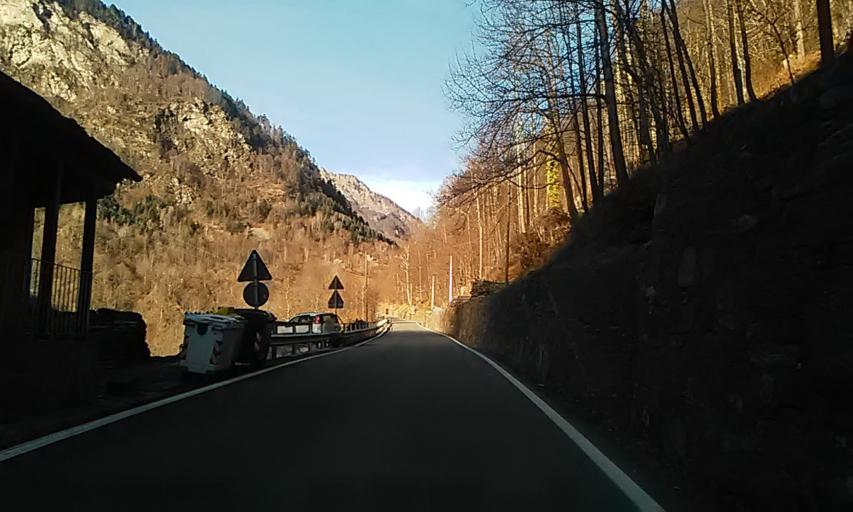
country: IT
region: Piedmont
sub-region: Provincia di Vercelli
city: Boccioleto
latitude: 45.8320
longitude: 8.0907
